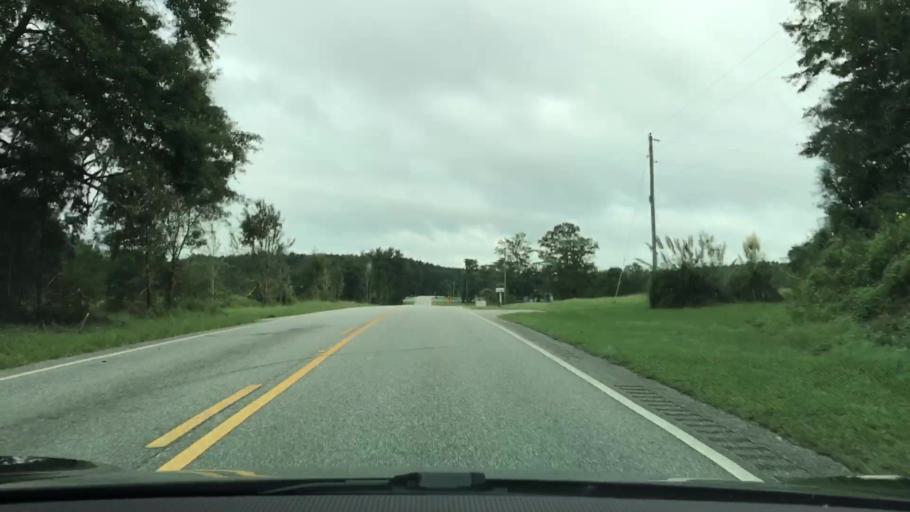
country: US
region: Alabama
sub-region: Geneva County
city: Samson
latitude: 31.0141
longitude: -86.1261
